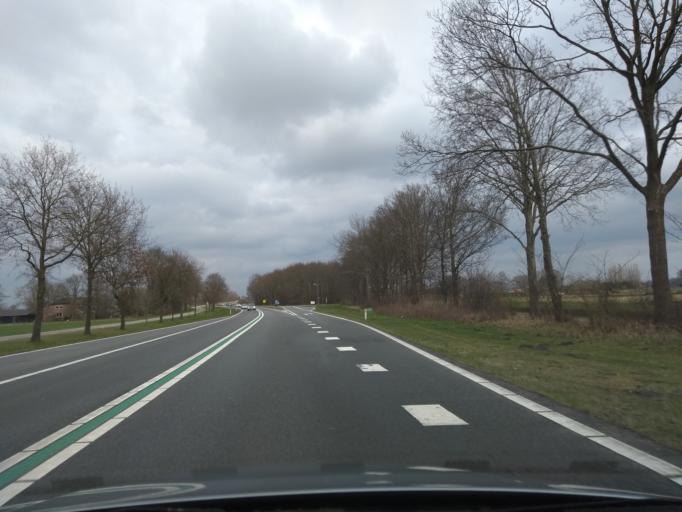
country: NL
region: Overijssel
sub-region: Gemeente Staphorst
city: Staphorst
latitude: 52.5866
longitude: 6.2146
